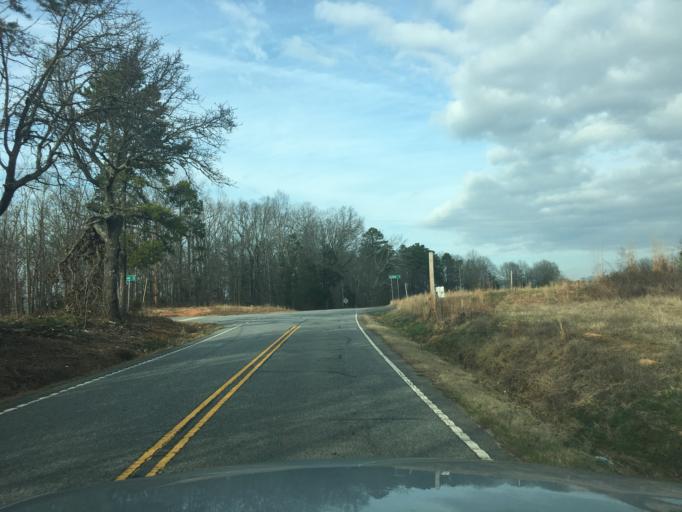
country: US
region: South Carolina
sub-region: Abbeville County
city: Lake Secession
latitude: 34.3771
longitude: -82.5196
